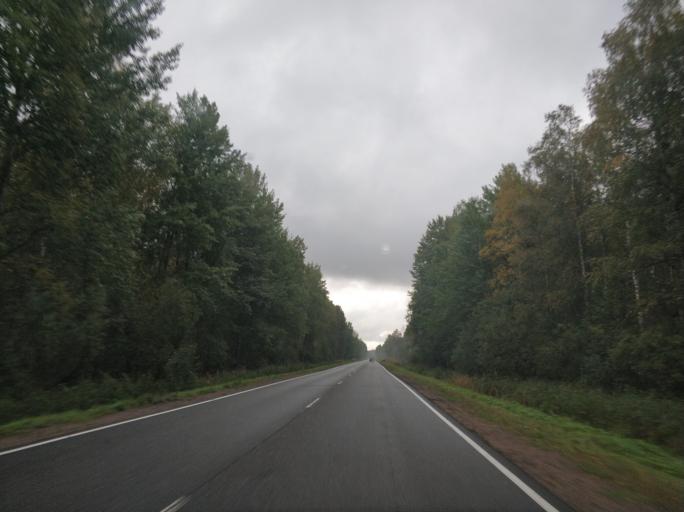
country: RU
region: Leningrad
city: Borisova Griva
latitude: 60.1210
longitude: 30.9635
